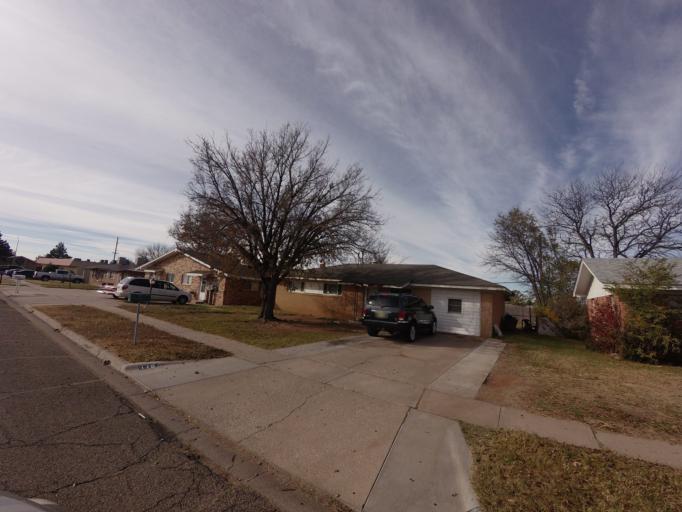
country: US
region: New Mexico
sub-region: Curry County
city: Clovis
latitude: 34.4203
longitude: -103.2235
